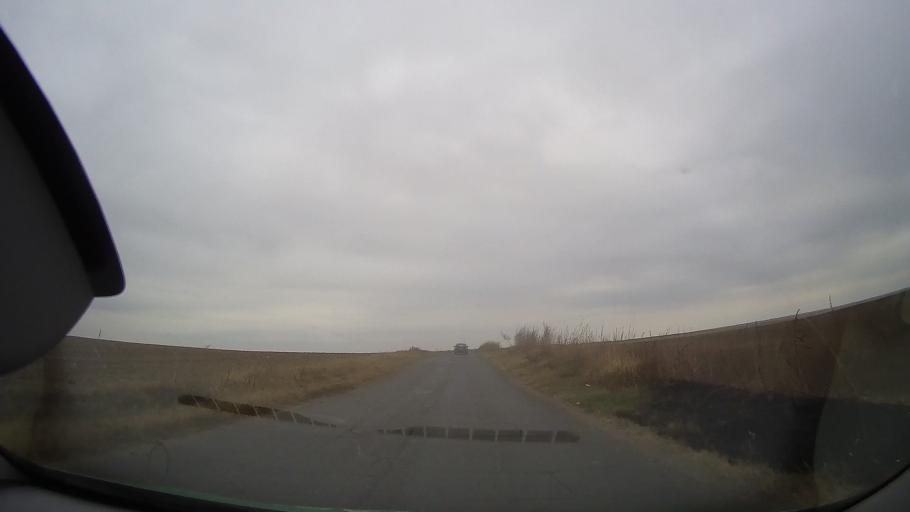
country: RO
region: Buzau
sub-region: Comuna Rusetu
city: Rusetu
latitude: 44.9660
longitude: 27.1999
